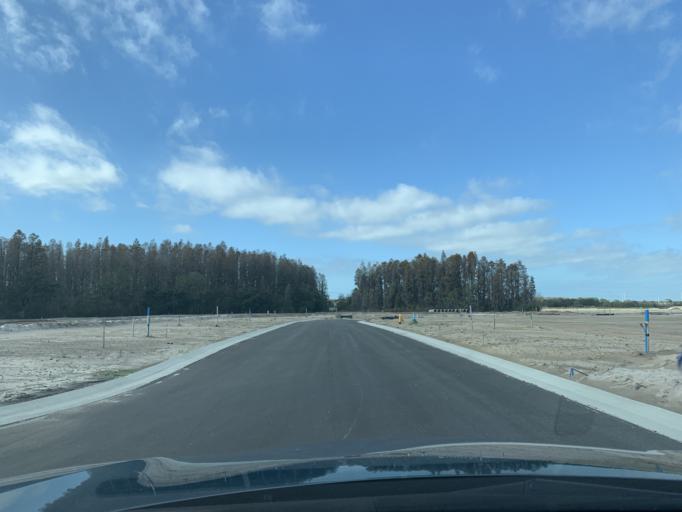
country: US
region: Florida
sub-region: Pasco County
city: Trinity
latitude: 28.1980
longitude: -82.6744
